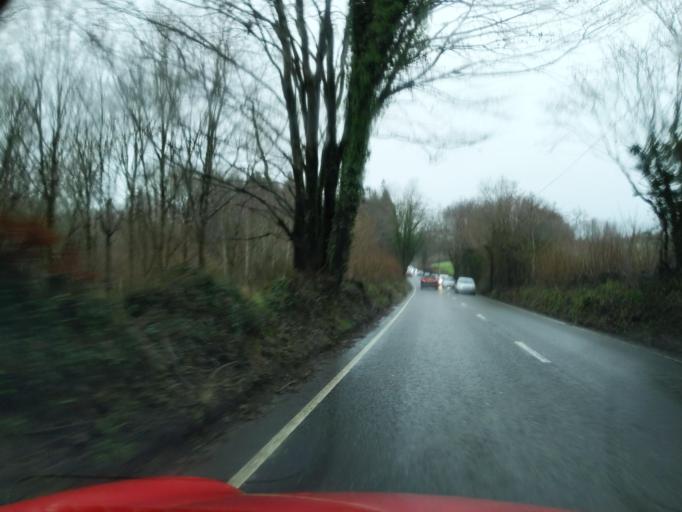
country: GB
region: England
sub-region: Cornwall
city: South Hill
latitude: 50.5792
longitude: -4.3331
